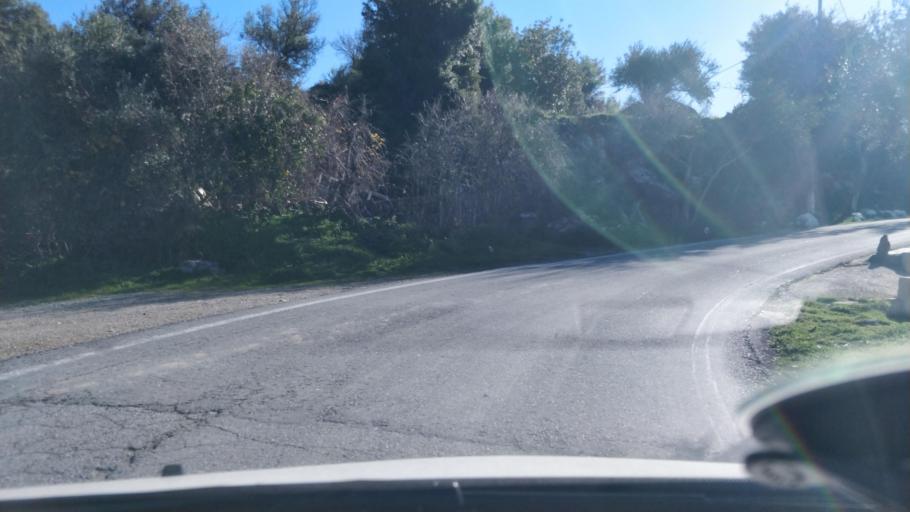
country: GR
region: Crete
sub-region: Nomos Lasithiou
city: Kritsa
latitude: 35.0802
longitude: 25.5893
